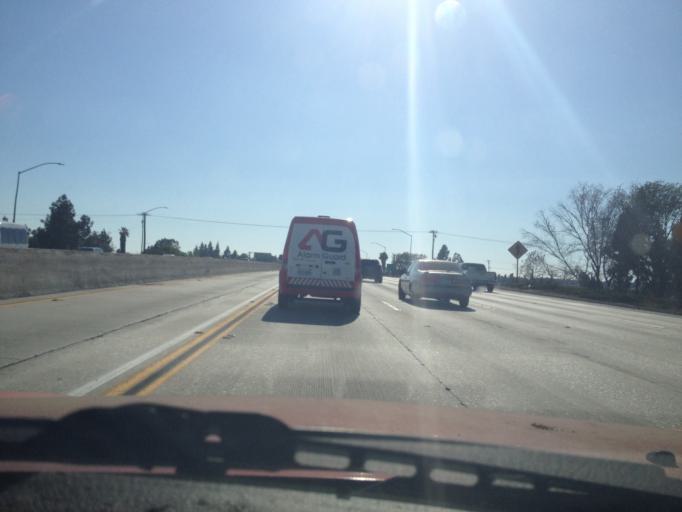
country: US
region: California
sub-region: Los Angeles County
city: Artesia
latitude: 33.8766
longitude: -118.0692
